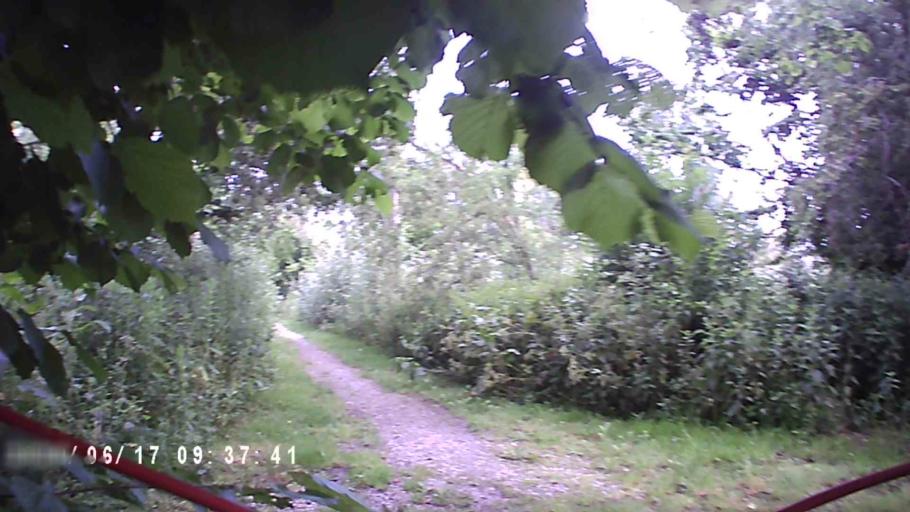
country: NL
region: Groningen
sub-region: Gemeente De Marne
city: Ulrum
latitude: 53.3495
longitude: 6.3678
